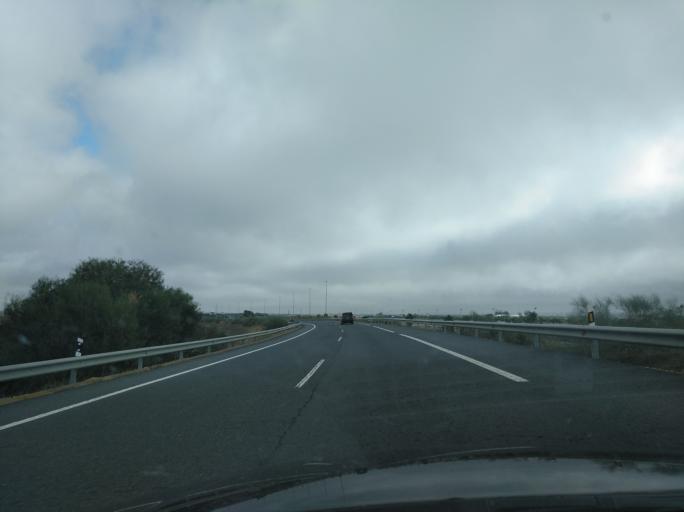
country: ES
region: Andalusia
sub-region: Provincia de Huelva
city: San Juan del Puerto
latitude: 37.3119
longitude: -6.8769
